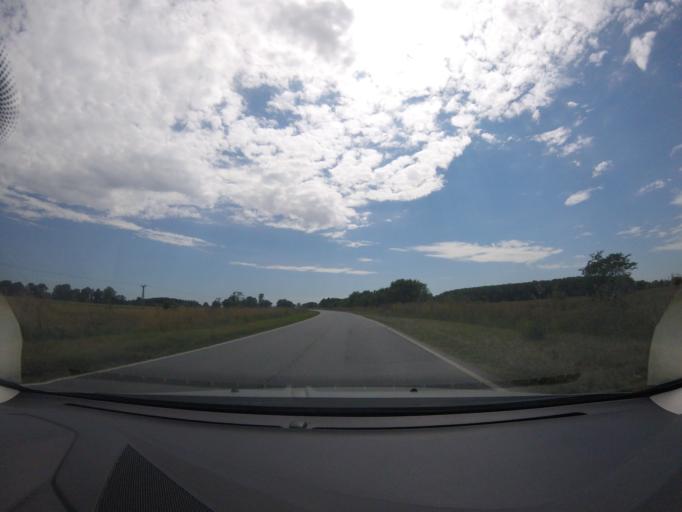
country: AR
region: Buenos Aires
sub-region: Partido de Tandil
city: Tandil
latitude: -37.2573
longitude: -59.1333
